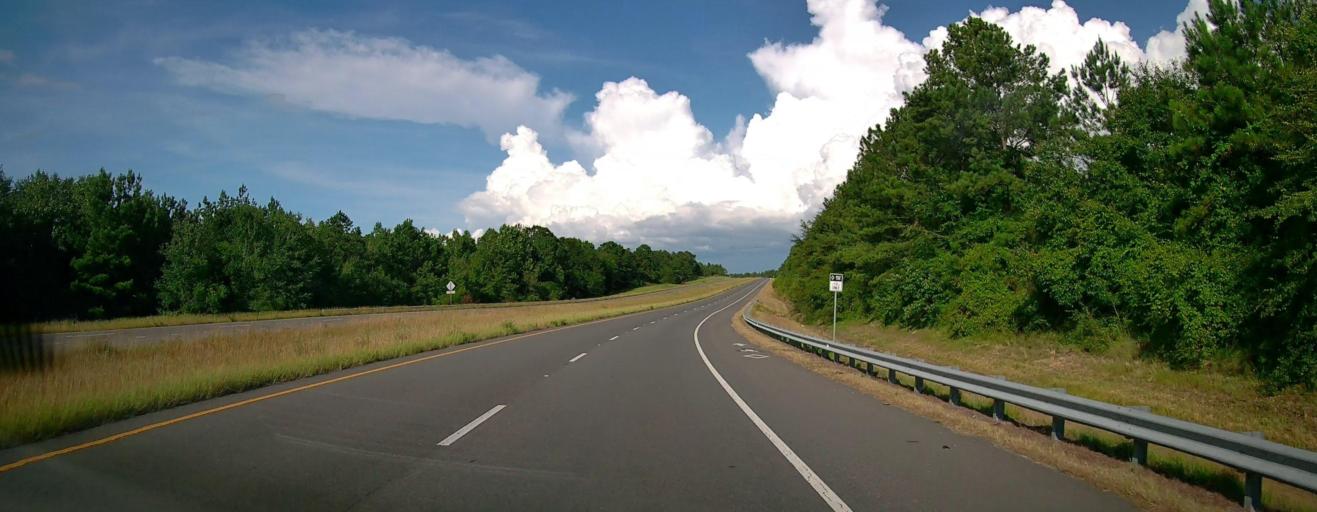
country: US
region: Georgia
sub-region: Talbot County
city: Talbotton
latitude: 32.5824
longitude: -84.5203
